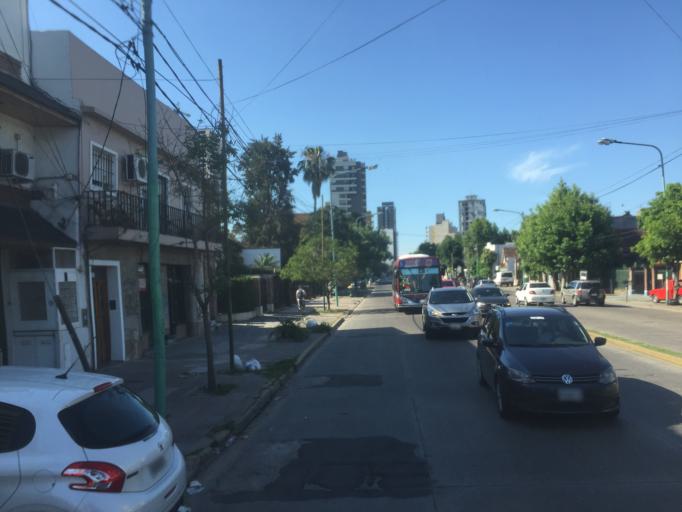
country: AR
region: Buenos Aires
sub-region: Partido de Lomas de Zamora
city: Lomas de Zamora
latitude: -34.7678
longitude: -58.3966
